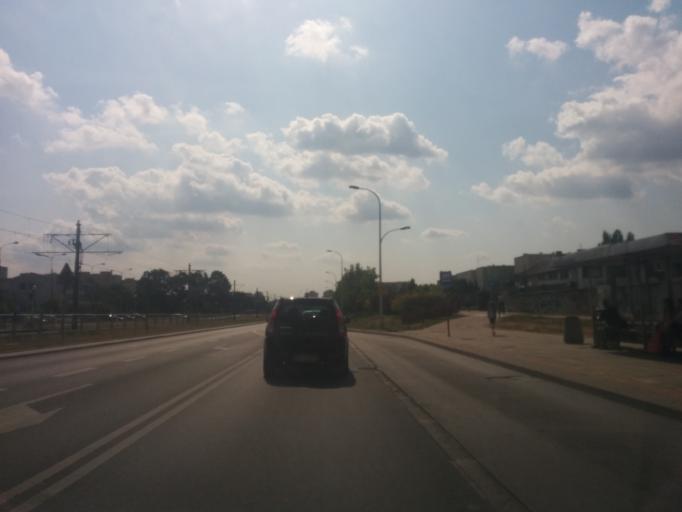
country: PL
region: Masovian Voivodeship
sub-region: Warszawa
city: Bialoleka
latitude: 52.3223
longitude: 20.9446
